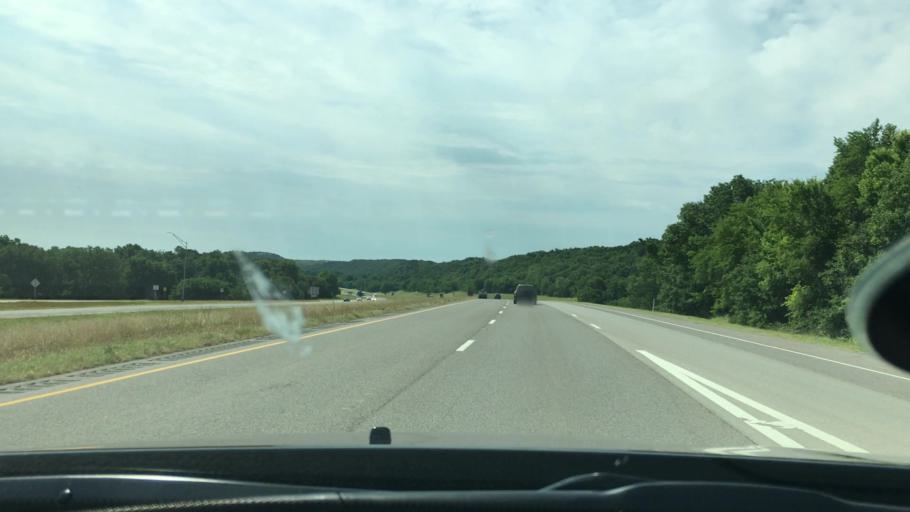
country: US
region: Oklahoma
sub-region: Murray County
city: Davis
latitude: 34.4750
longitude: -97.1564
